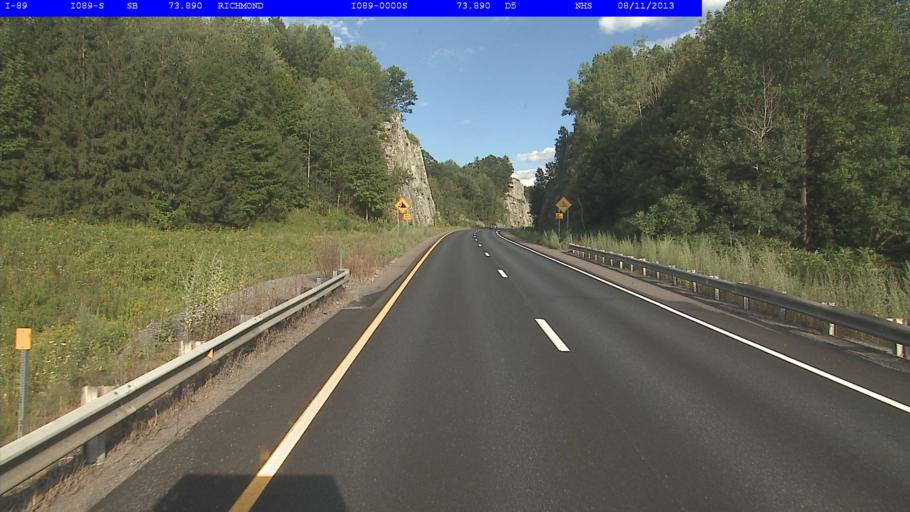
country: US
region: Vermont
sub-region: Chittenden County
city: Jericho
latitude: 44.3877
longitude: -72.9414
